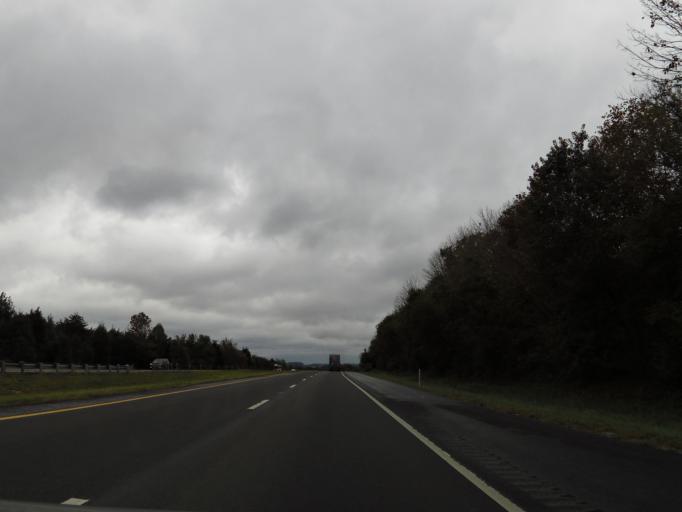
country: US
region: Tennessee
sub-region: Loudon County
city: Loudon
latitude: 35.7484
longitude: -84.3816
